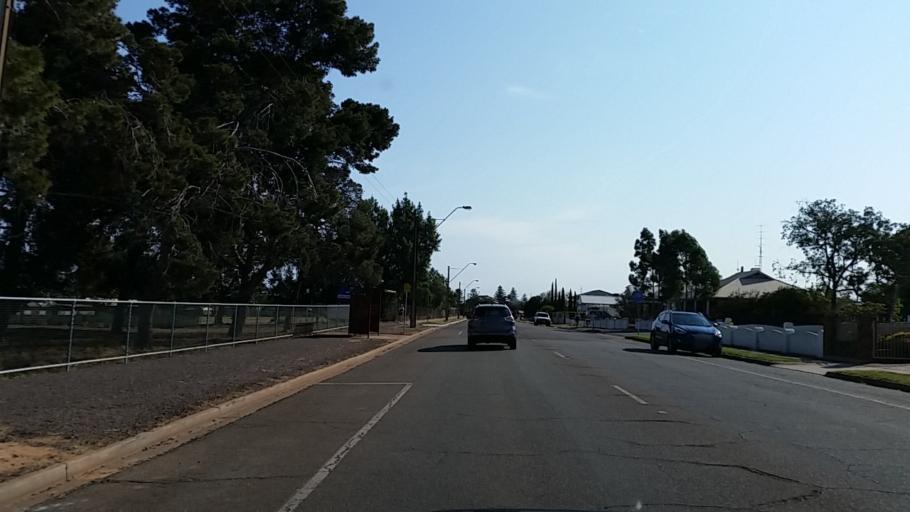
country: AU
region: South Australia
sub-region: Whyalla
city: Whyalla
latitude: -33.0404
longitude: 137.5792
